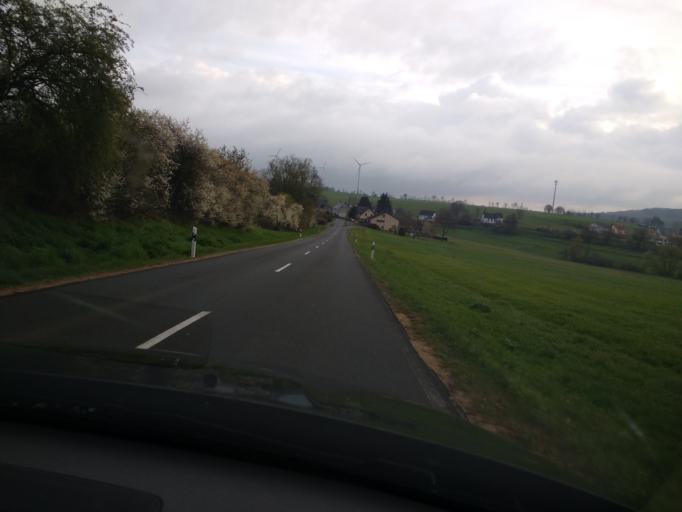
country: DE
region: Rheinland-Pfalz
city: Kalenborn-Scheuern
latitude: 50.2551
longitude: 6.5919
